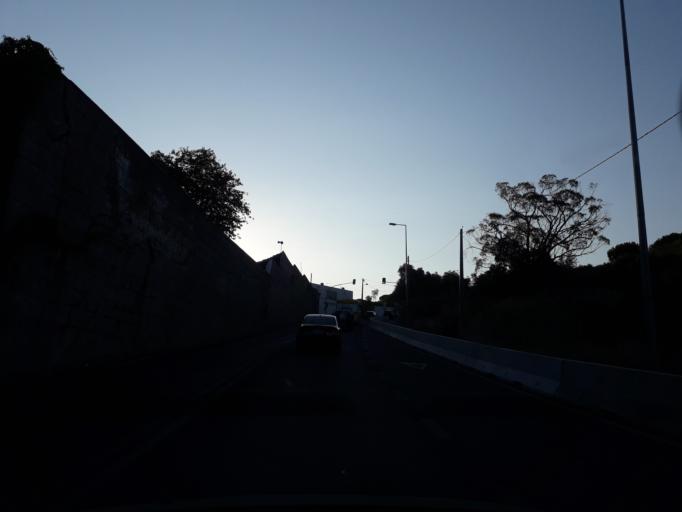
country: PT
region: Lisbon
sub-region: Odivelas
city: Pontinha
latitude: 38.7716
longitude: -9.2018
